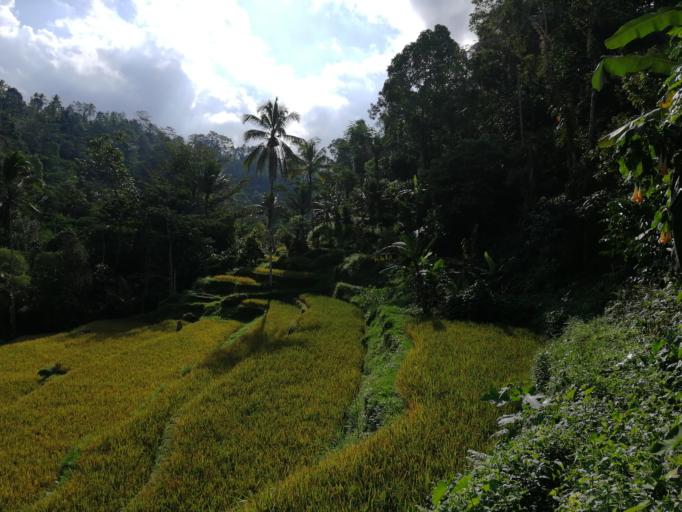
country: ID
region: Bali
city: Peneng
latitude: -8.3629
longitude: 115.1984
